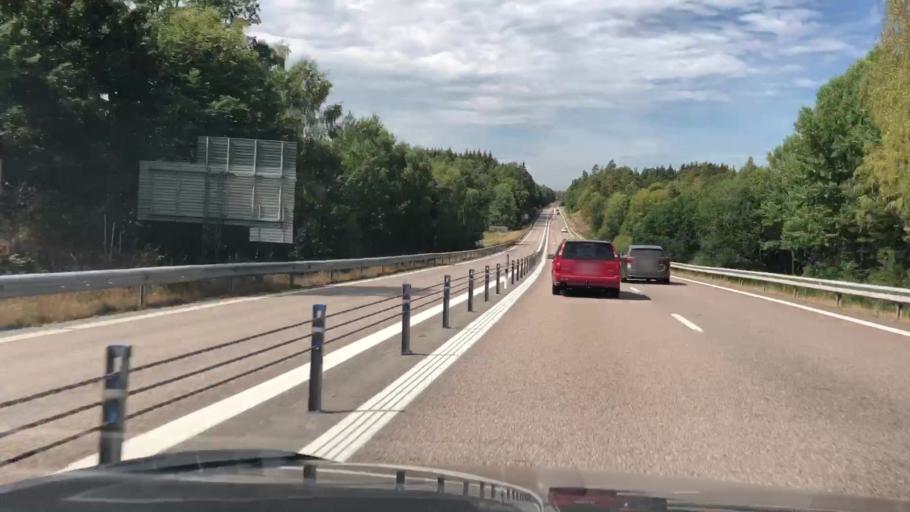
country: SE
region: Blekinge
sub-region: Ronneby Kommun
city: Kallinge
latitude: 56.2139
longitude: 15.3106
